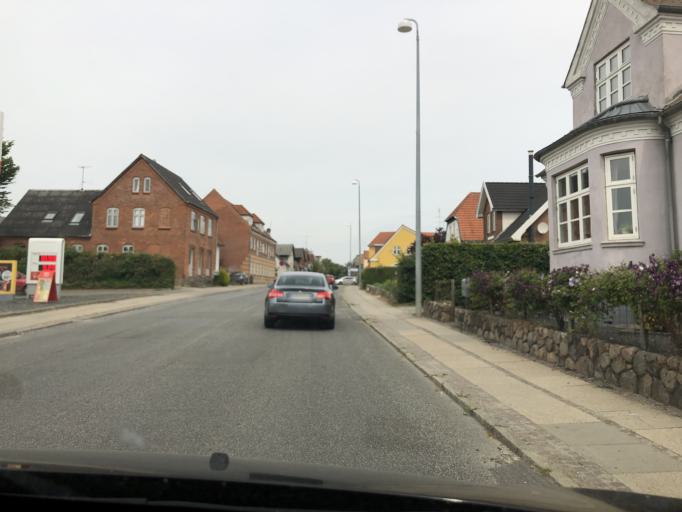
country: DK
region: South Denmark
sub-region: Assens Kommune
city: Glamsbjerg
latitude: 55.2762
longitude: 10.1072
